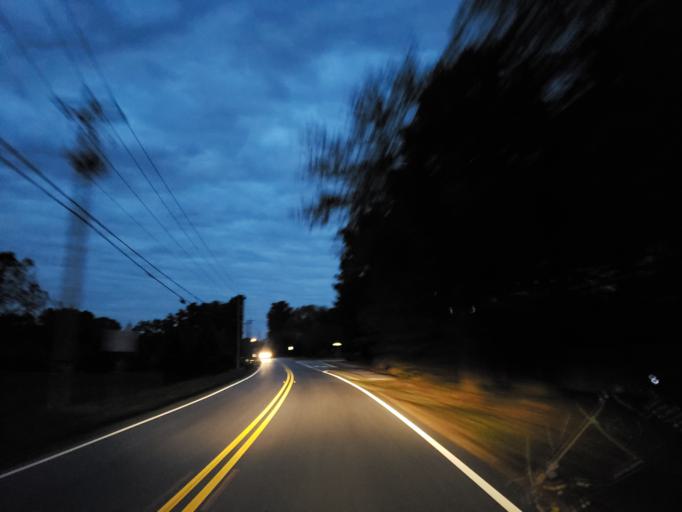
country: US
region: Georgia
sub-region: Cobb County
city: Powder Springs
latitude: 33.8955
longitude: -84.7085
